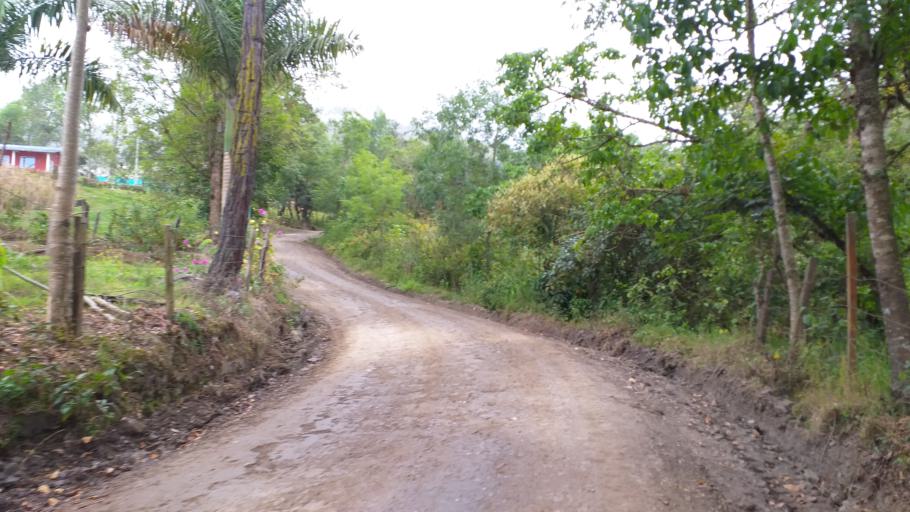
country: CO
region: Cundinamarca
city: Tenza
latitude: 5.0918
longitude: -73.4533
